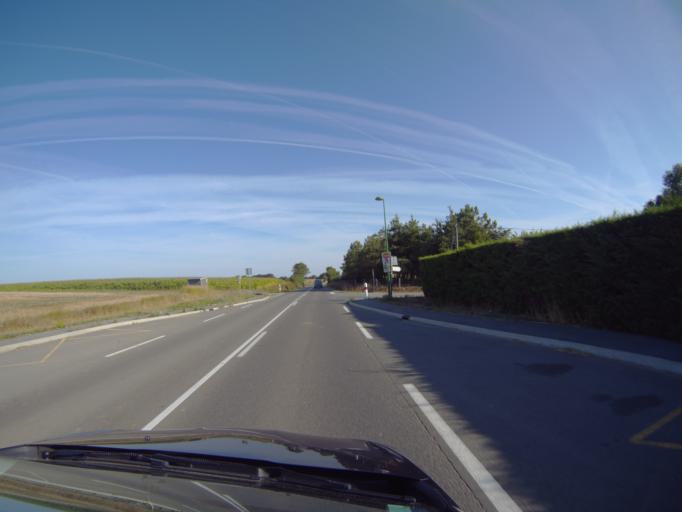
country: FR
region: Pays de la Loire
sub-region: Departement de la Vendee
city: Jard-sur-Mer
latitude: 46.4439
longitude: -1.5793
